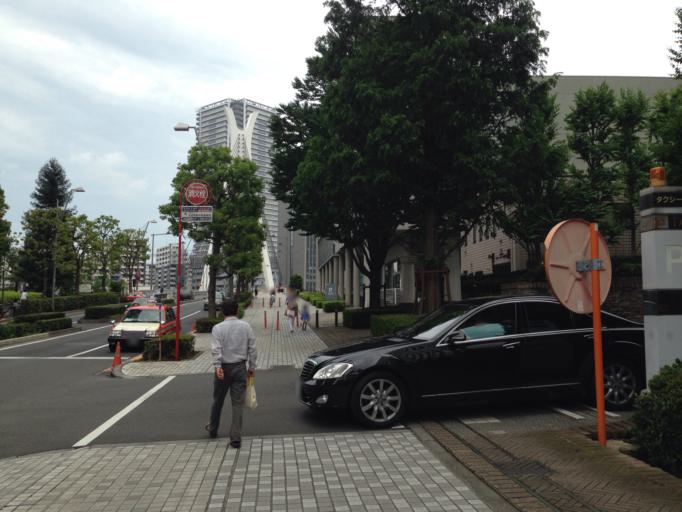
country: JP
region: Tokyo
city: Tokyo
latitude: 35.6699
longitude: 139.7850
